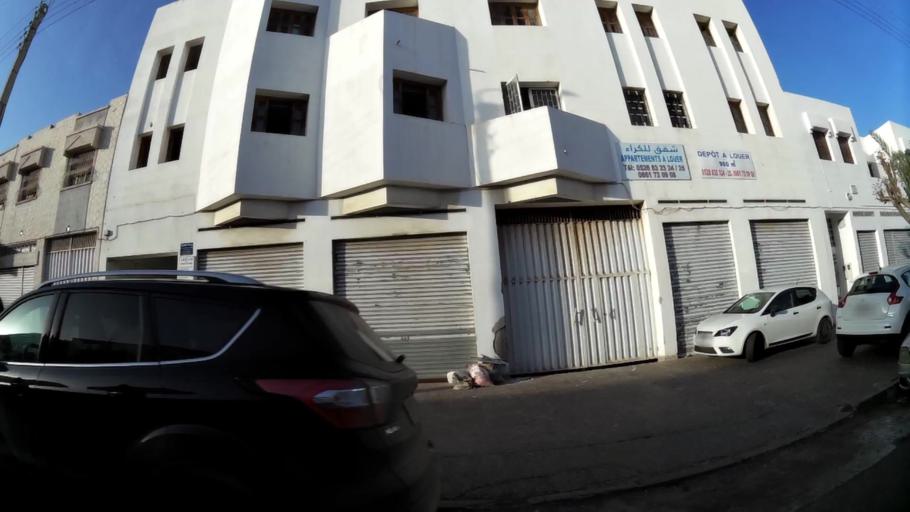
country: MA
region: Oued ed Dahab-Lagouira
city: Dakhla
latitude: 30.4138
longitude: -9.5502
